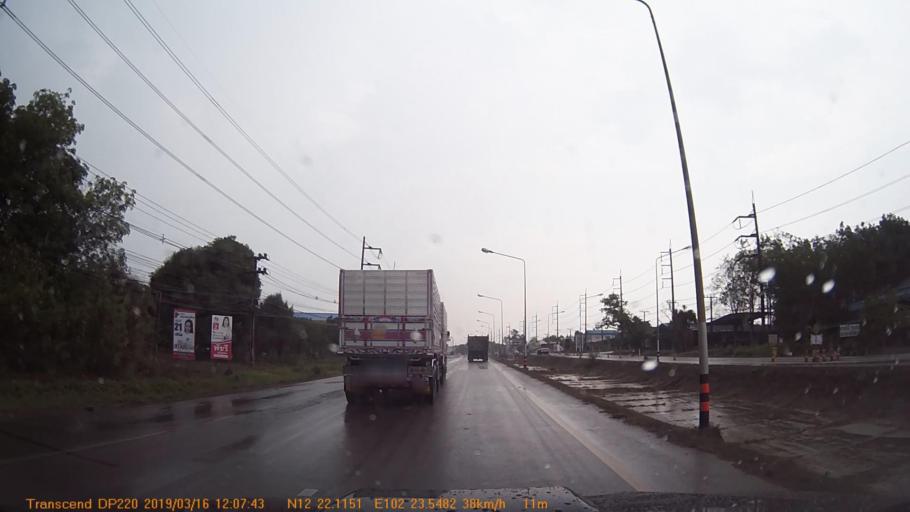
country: TH
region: Trat
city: Khao Saming
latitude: 12.3672
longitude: 102.4031
